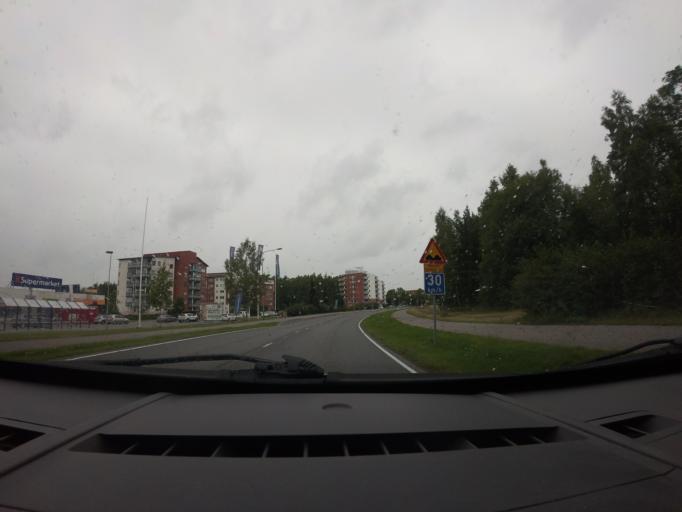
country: FI
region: Varsinais-Suomi
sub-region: Turku
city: Turku
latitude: 60.4177
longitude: 22.3023
